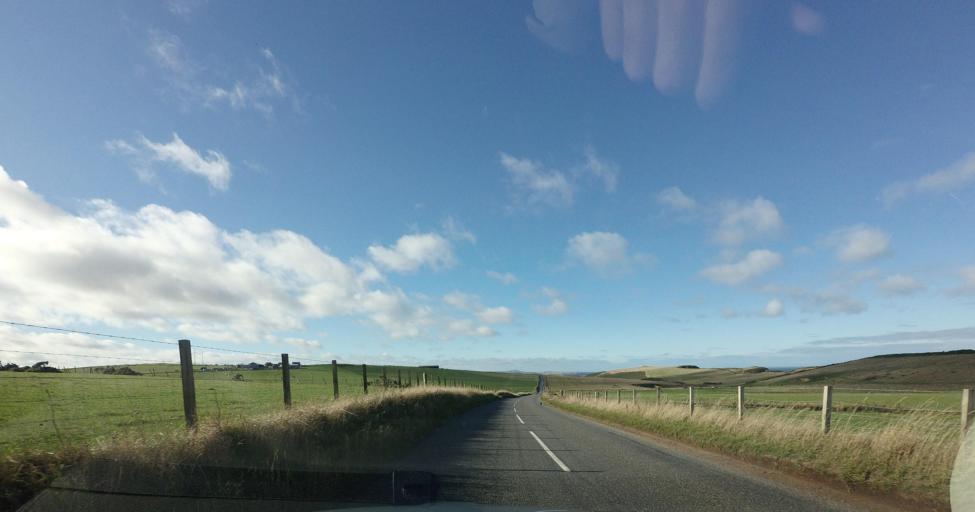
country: GB
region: Scotland
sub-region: Aberdeenshire
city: Macduff
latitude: 57.6640
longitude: -2.3886
